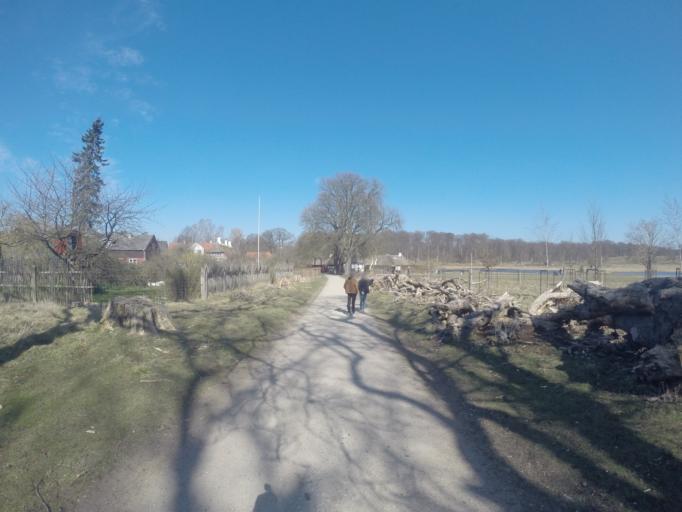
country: DK
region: Capital Region
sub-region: Rudersdal Kommune
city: Trorod
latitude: 55.7981
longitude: 12.5449
